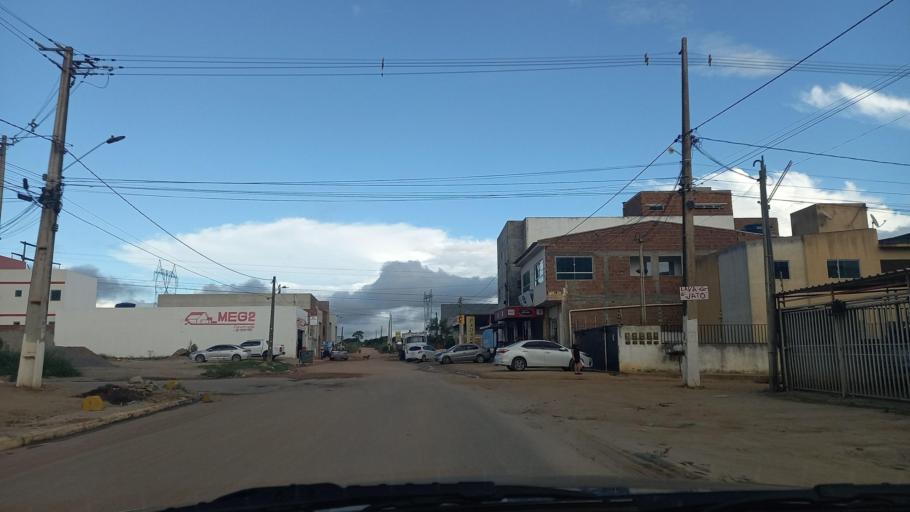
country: BR
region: Pernambuco
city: Garanhuns
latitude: -8.9133
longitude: -36.4784
